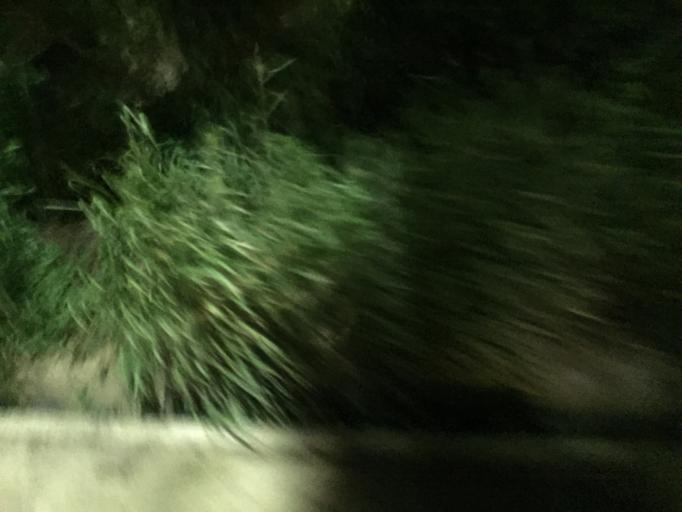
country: TW
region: Taiwan
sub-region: Hsinchu
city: Hsinchu
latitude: 24.7540
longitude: 120.9561
